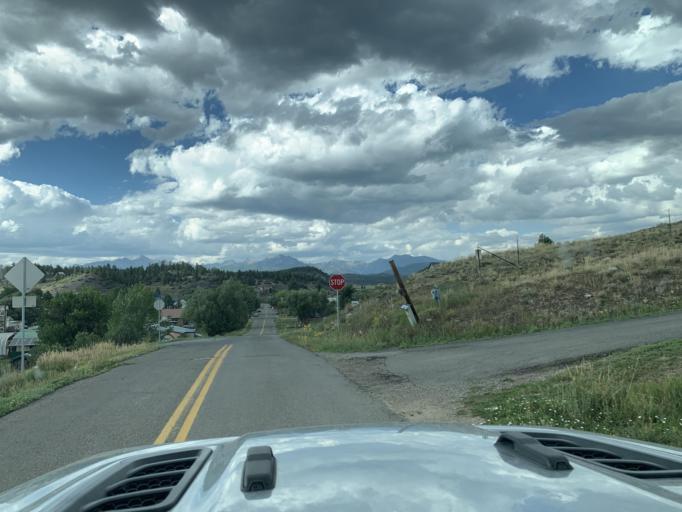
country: US
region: Colorado
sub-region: Archuleta County
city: Pagosa Springs
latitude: 37.2612
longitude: -107.0158
